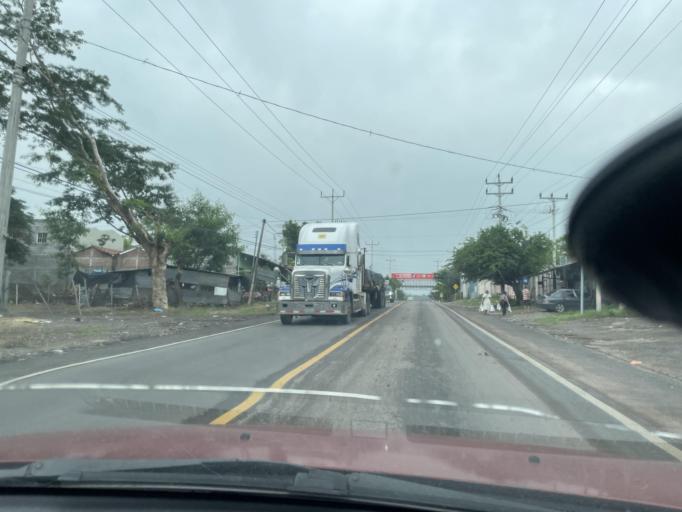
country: SV
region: San Miguel
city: San Miguel
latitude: 13.5101
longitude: -88.1514
